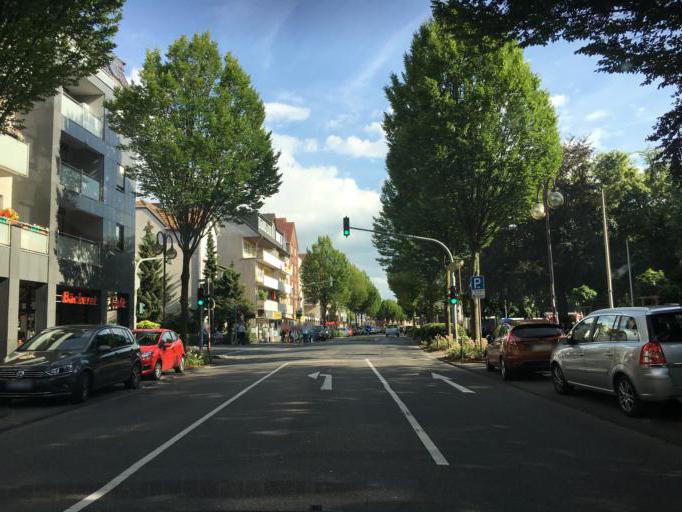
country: DE
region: North Rhine-Westphalia
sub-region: Regierungsbezirk Koln
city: Kerpen
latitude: 50.9124
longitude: 6.7112
